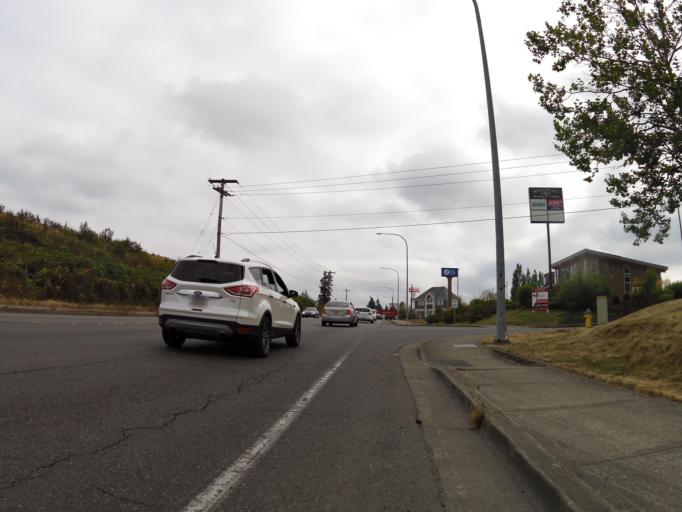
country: US
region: Washington
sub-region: Kitsap County
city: Navy Yard City
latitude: 47.5685
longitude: -122.6846
